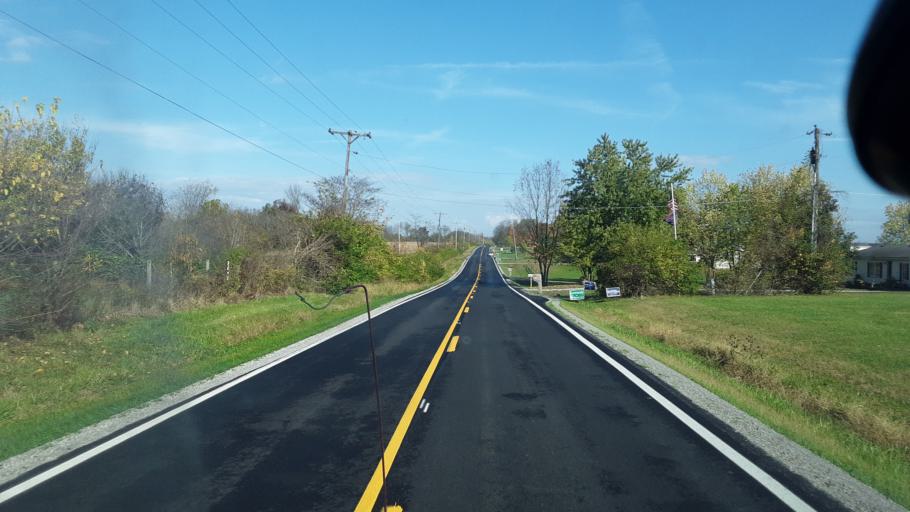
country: US
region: Ohio
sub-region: Highland County
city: Leesburg
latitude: 39.3698
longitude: -83.5932
